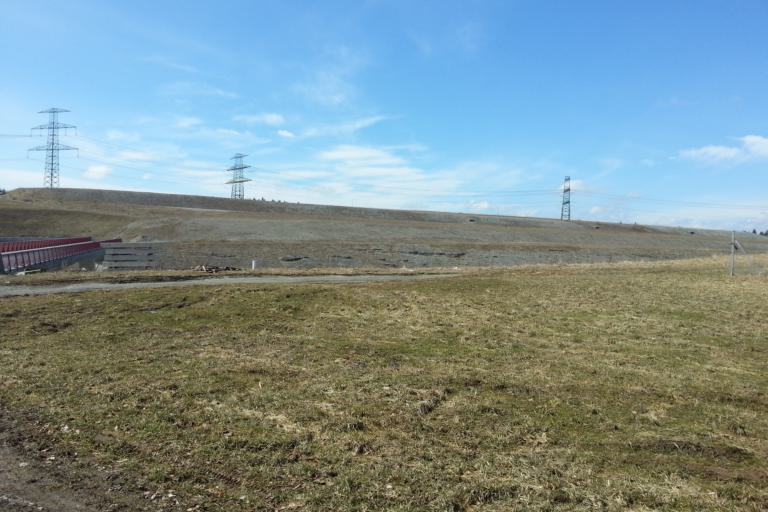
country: DE
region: Thuringia
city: Schalkau
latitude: 50.4119
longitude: 11.0272
